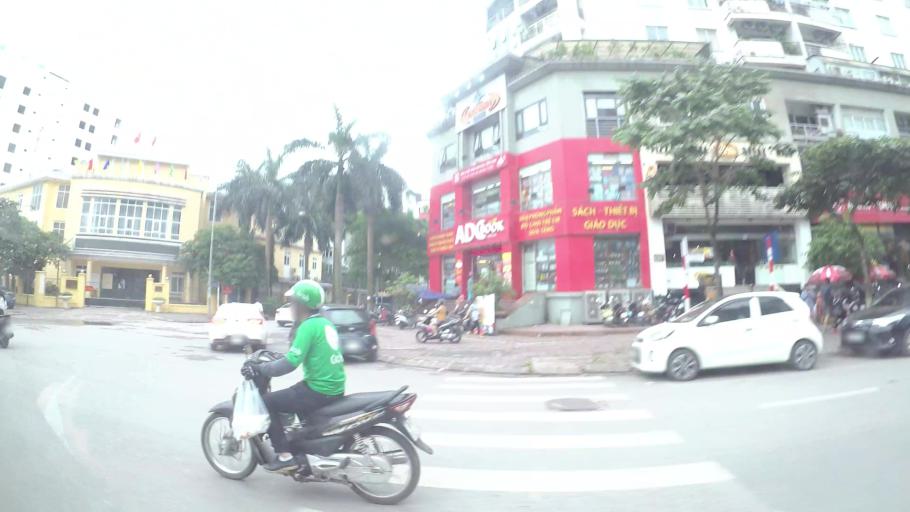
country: VN
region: Ha Noi
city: Cau Giay
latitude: 21.0319
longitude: 105.7883
